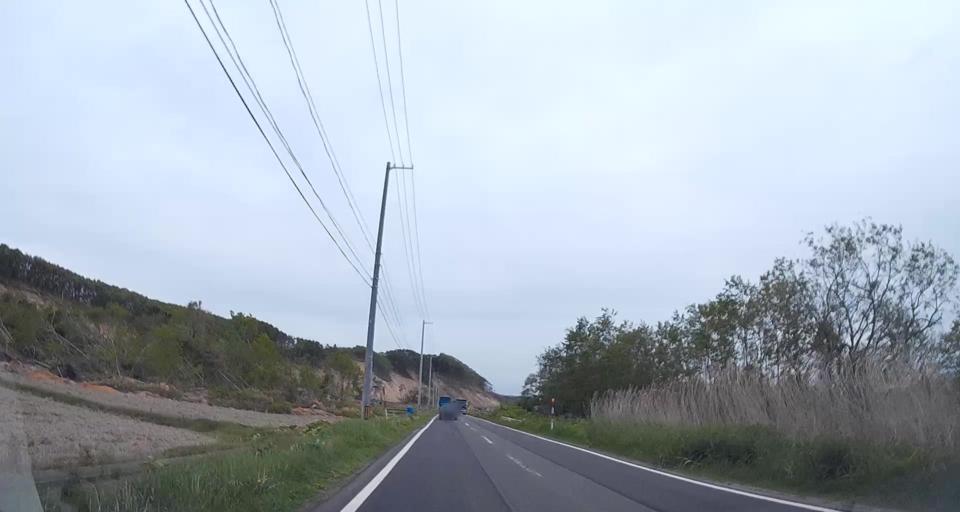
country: JP
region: Hokkaido
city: Chitose
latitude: 42.7448
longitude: 141.9070
